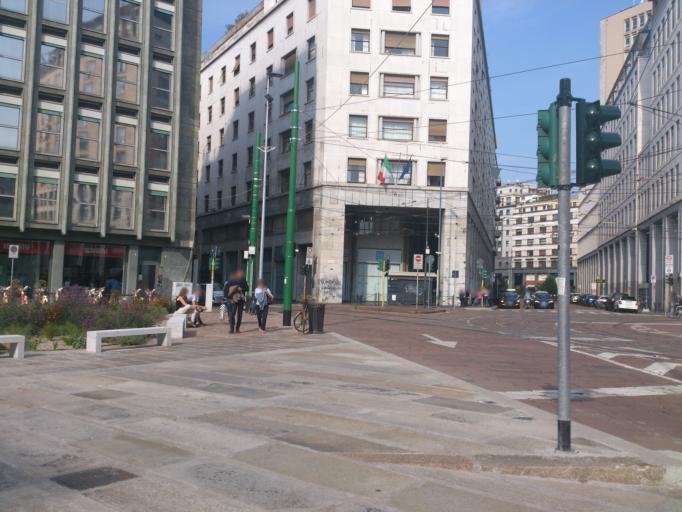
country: IT
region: Lombardy
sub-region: Citta metropolitana di Milano
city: Milano
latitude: 45.4610
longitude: 9.1880
